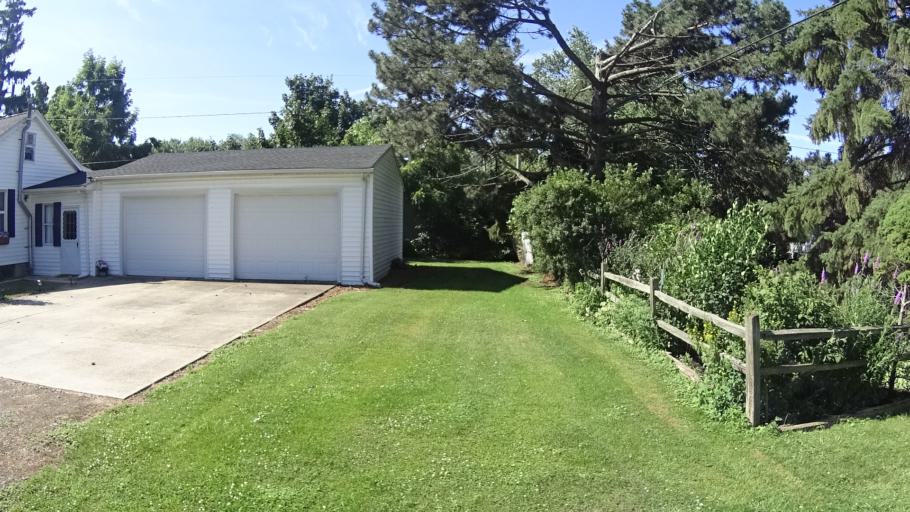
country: US
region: Ohio
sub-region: Ottawa County
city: Port Clinton
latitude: 41.4684
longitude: -82.8268
